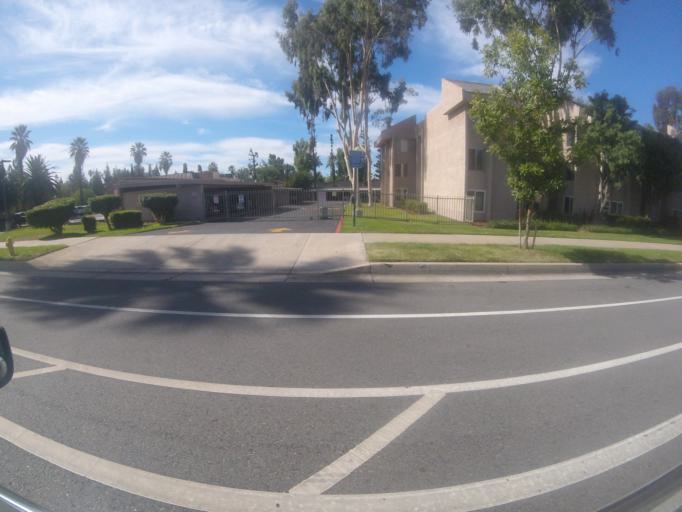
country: US
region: California
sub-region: San Bernardino County
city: Mentone
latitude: 34.0563
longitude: -117.1564
